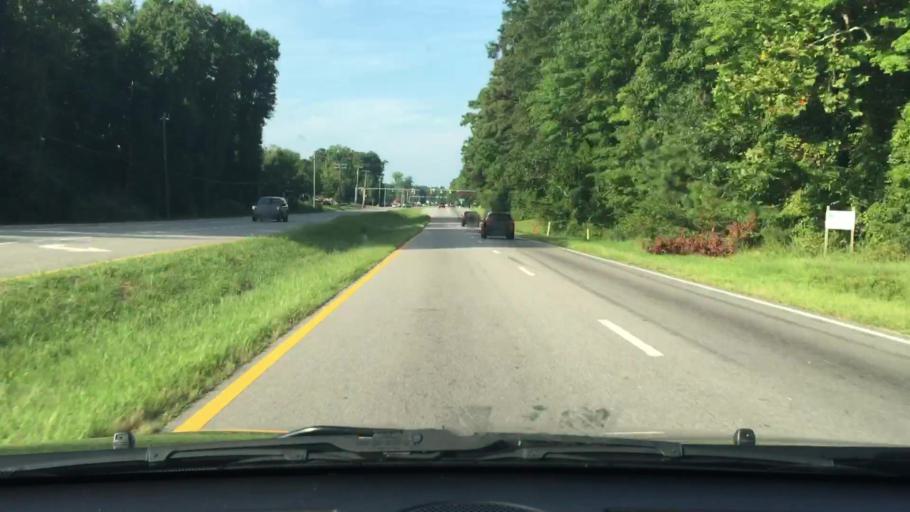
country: US
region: Virginia
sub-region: Isle of Wight County
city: Carrollton
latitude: 36.9560
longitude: -76.5267
